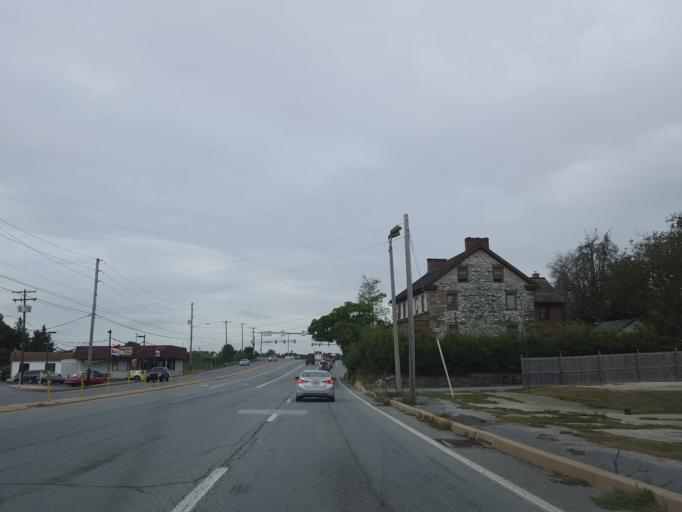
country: US
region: Pennsylvania
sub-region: York County
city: Shiloh
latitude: 39.9291
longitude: -76.8203
